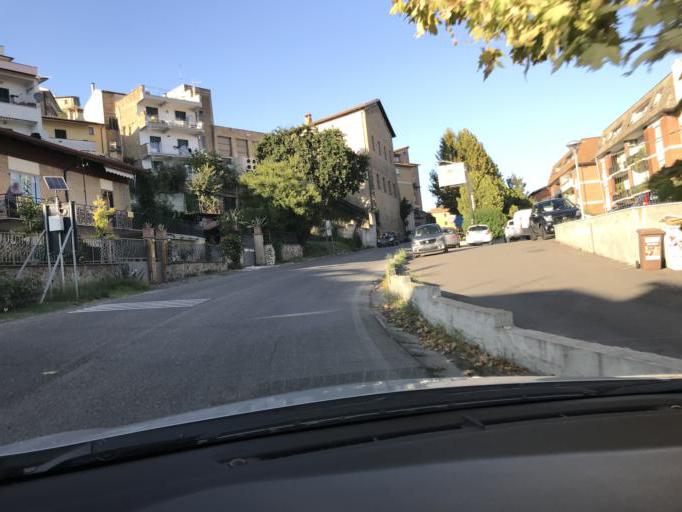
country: IT
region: Latium
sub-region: Provincia di Viterbo
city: Orte
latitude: 42.4574
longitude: 12.3871
